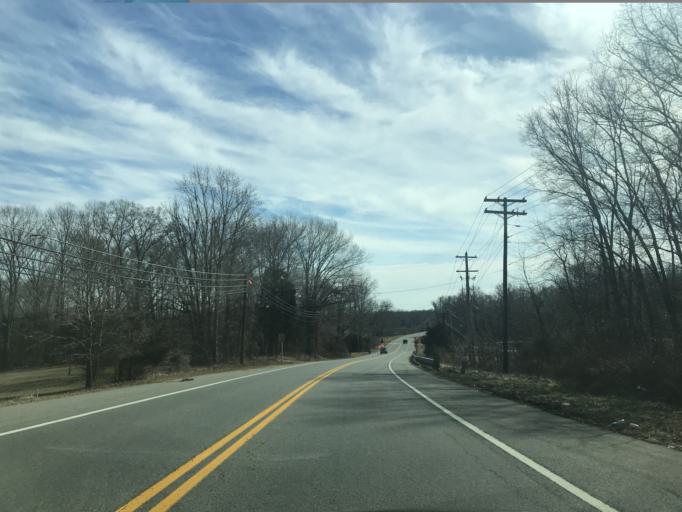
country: US
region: Maryland
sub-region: Charles County
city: Potomac Heights
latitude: 38.5964
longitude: -77.1243
